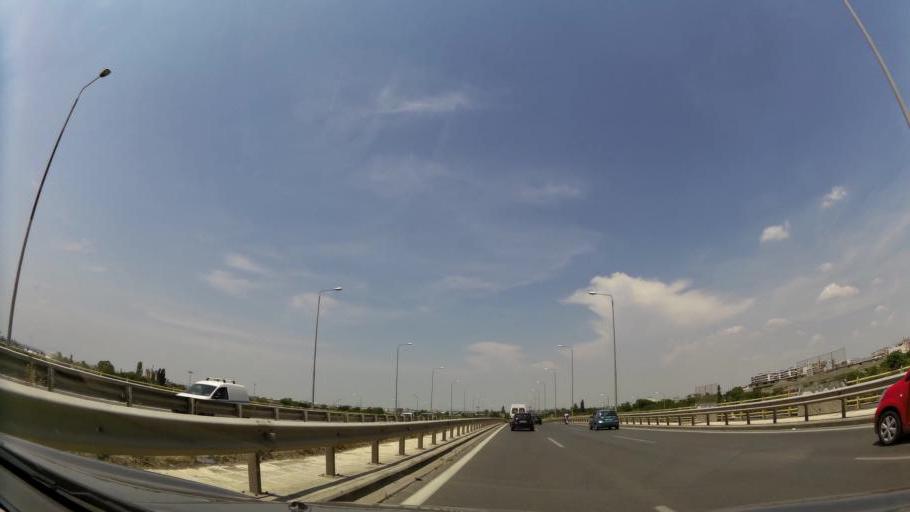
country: GR
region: Central Macedonia
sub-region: Nomos Thessalonikis
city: Ampelokipoi
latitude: 40.6486
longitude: 22.9108
